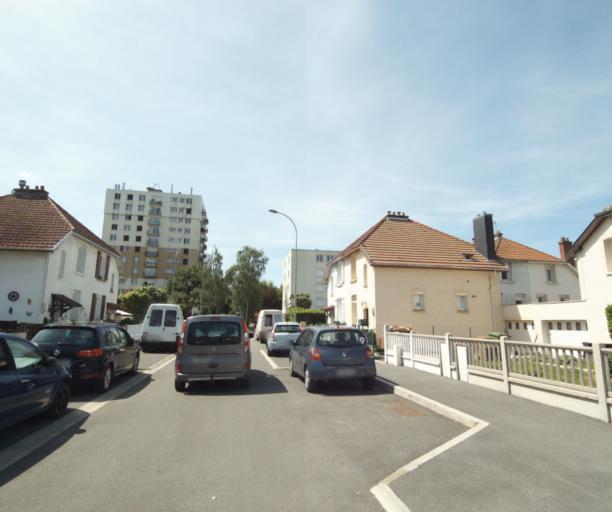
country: FR
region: Champagne-Ardenne
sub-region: Departement des Ardennes
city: Prix-les-Mezieres
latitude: 49.7621
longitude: 4.6932
